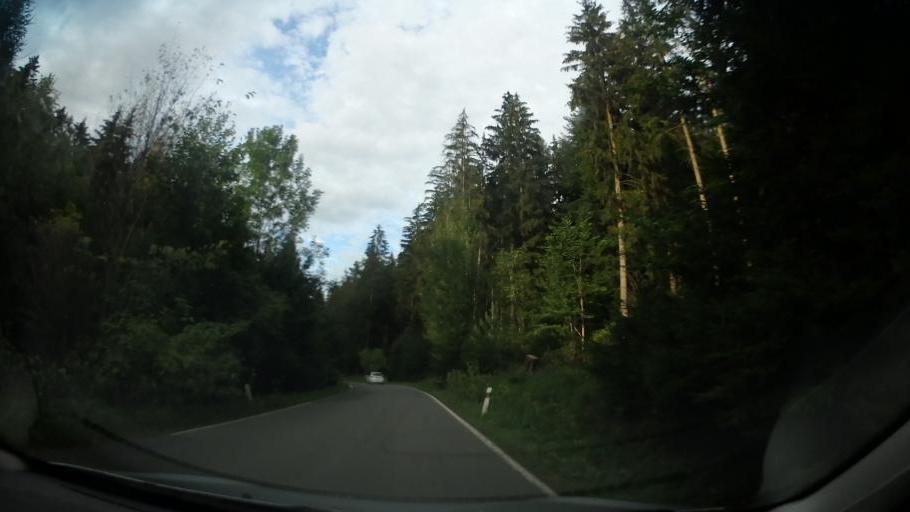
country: CZ
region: Olomoucky
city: Horni Stepanov
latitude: 49.5541
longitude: 16.7469
